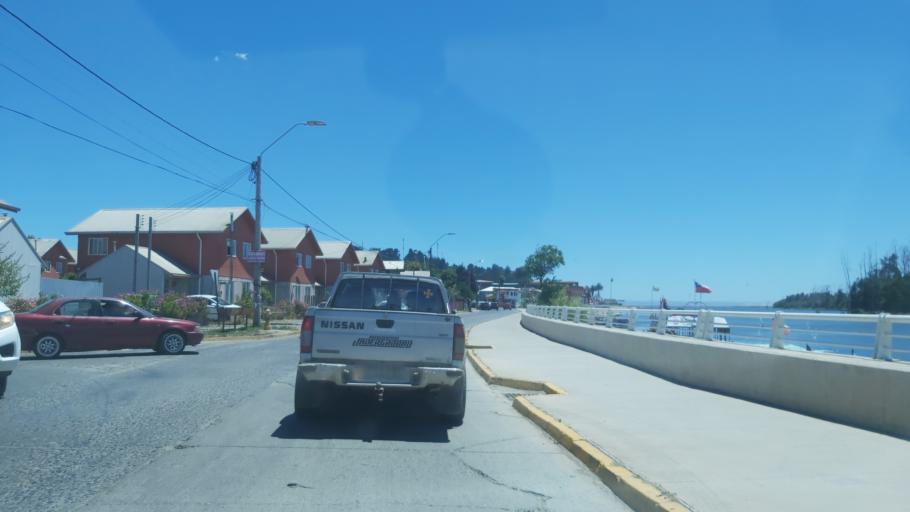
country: CL
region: Maule
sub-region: Provincia de Talca
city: Constitucion
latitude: -35.3337
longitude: -72.4056
